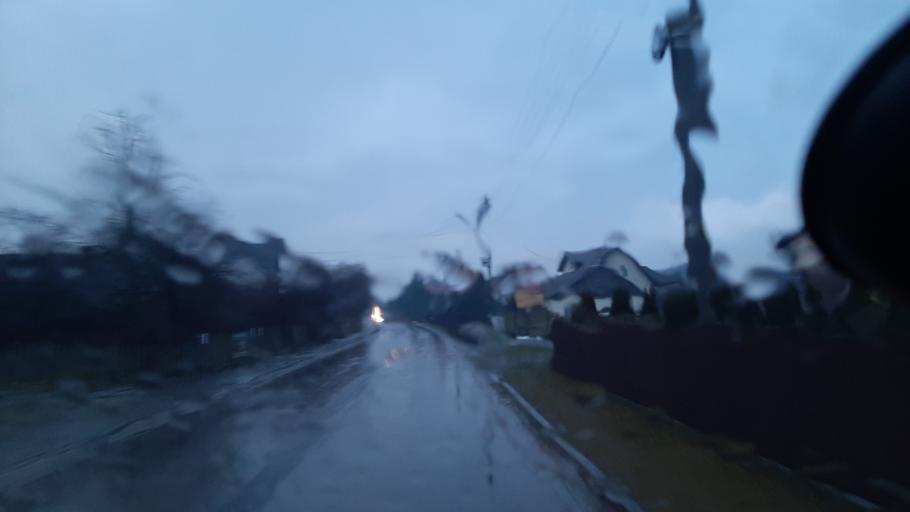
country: PL
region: Lublin Voivodeship
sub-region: Powiat lubartowski
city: Firlej
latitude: 51.5464
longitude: 22.5604
